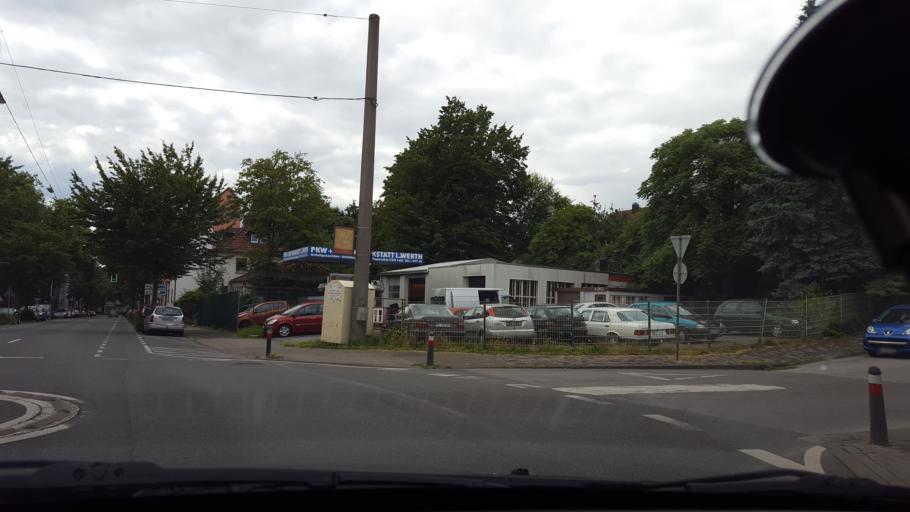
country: DE
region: North Rhine-Westphalia
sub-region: Regierungsbezirk Munster
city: Recklinghausen
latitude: 51.6147
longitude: 7.2101
